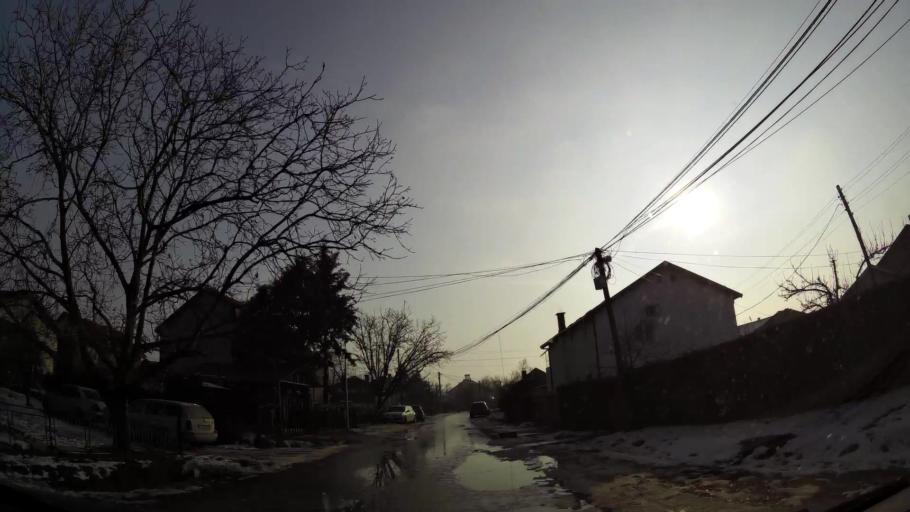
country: MK
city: Kadino
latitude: 41.9687
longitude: 21.6006
